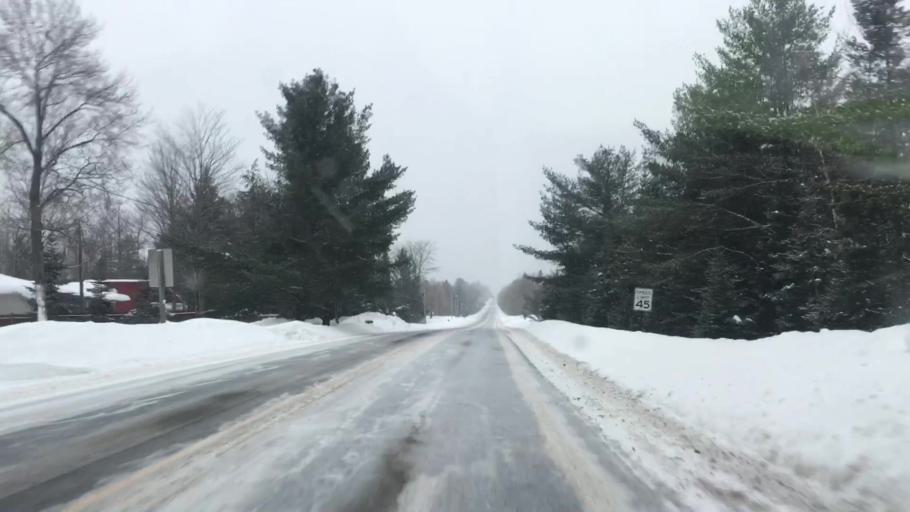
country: US
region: Maine
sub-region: Penobscot County
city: Medway
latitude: 45.5239
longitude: -68.3559
